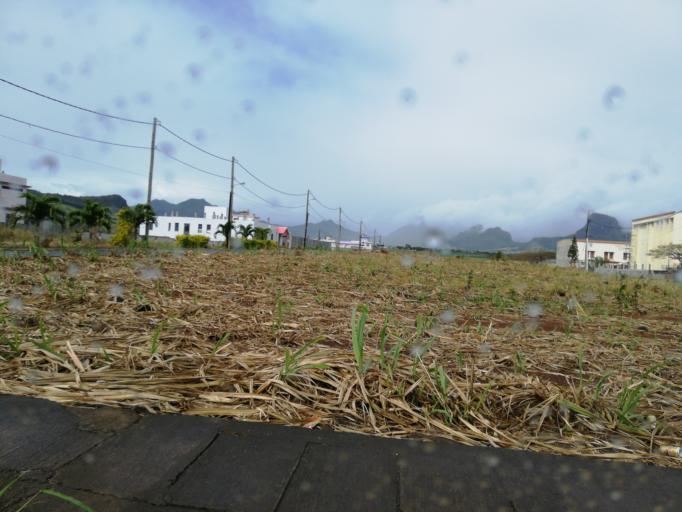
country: MU
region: Pamplemousses
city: Long Mountain
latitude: -20.1258
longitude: 57.5749
